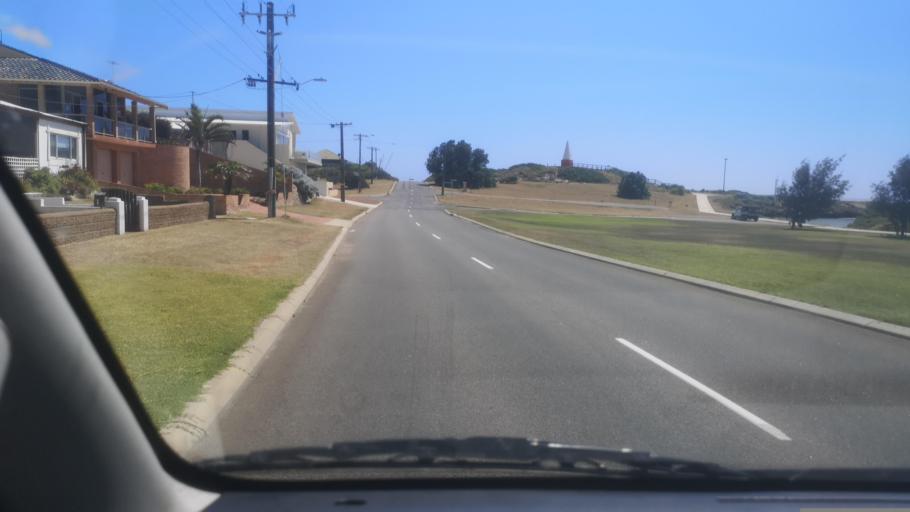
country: AU
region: Western Australia
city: Port Denison
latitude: -29.2767
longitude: 114.9173
